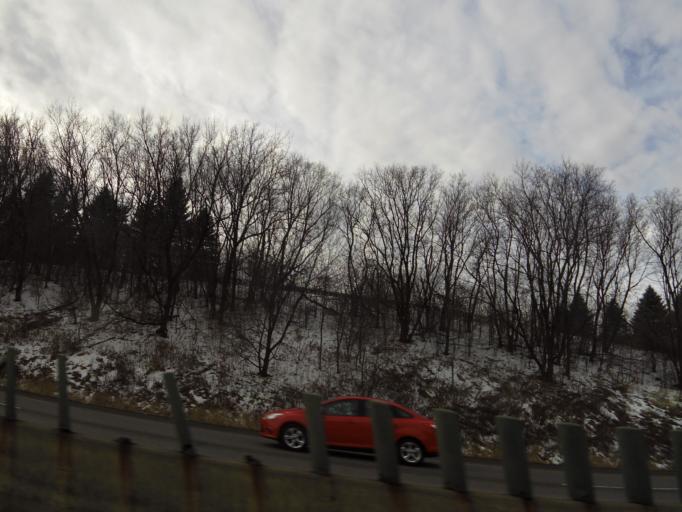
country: US
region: Minnesota
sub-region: Dakota County
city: Mendota Heights
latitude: 44.8921
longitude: -93.1311
